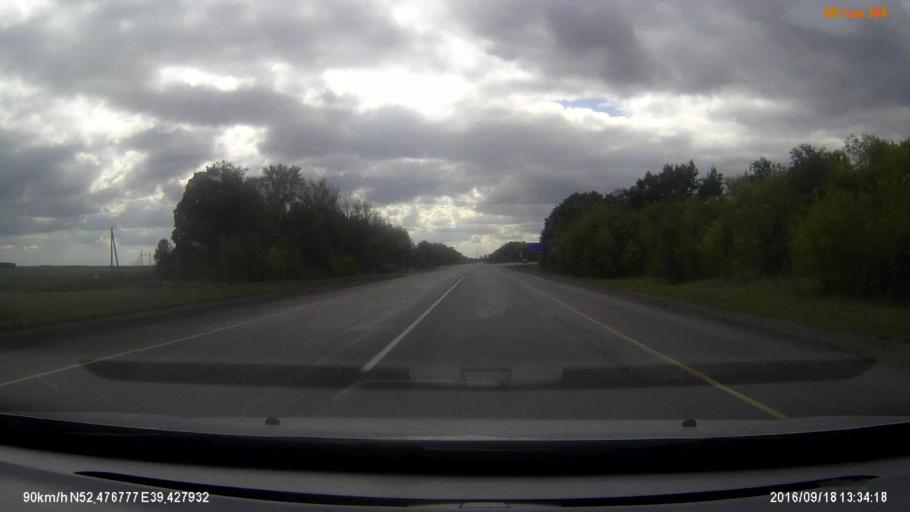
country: RU
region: Lipetsk
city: Borinskoye
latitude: 52.4866
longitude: 39.4403
